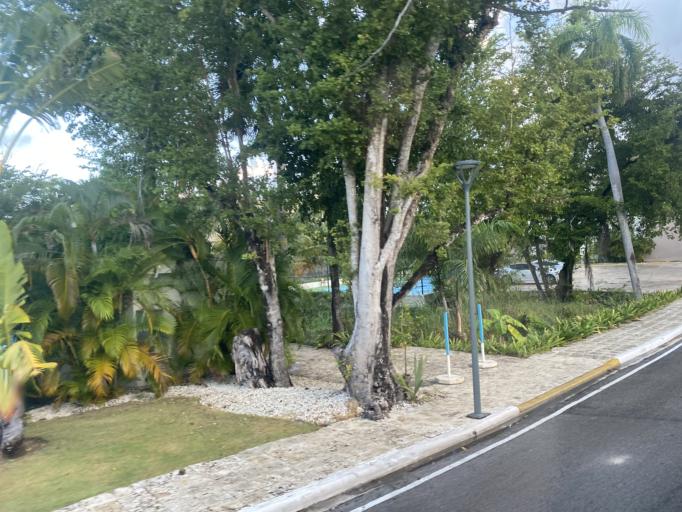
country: DO
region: San Juan
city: Punta Cana
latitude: 18.7272
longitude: -68.4705
